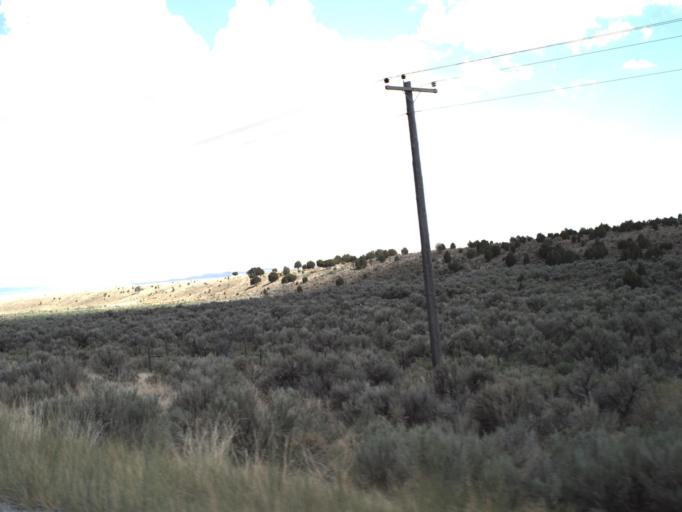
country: US
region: Idaho
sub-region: Minidoka County
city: Rupert
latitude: 41.9726
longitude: -113.1521
